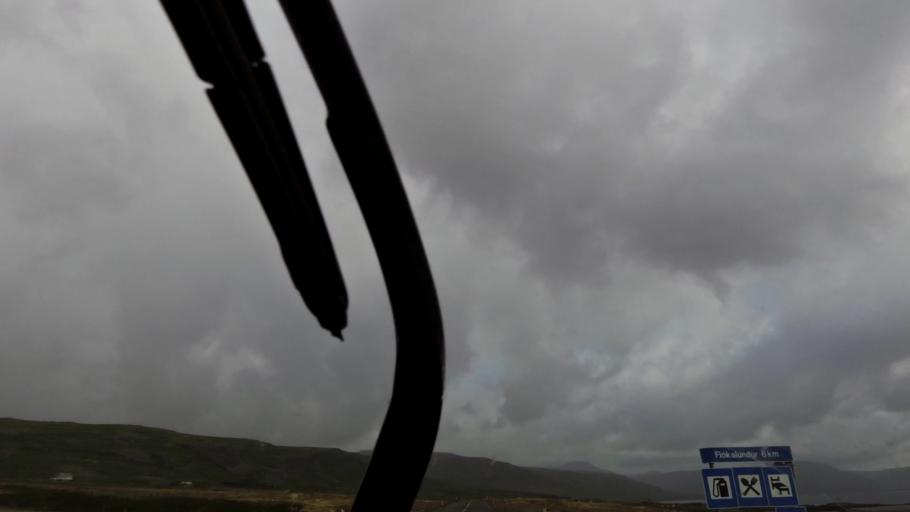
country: IS
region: Westfjords
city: Isafjoerdur
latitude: 65.5307
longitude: -23.1984
